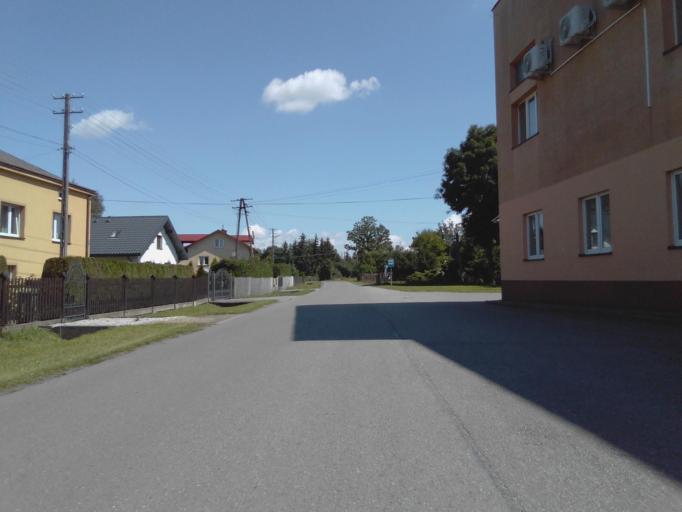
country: PL
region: Subcarpathian Voivodeship
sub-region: Powiat krosnienski
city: Jedlicze
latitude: 49.7462
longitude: 21.6343
